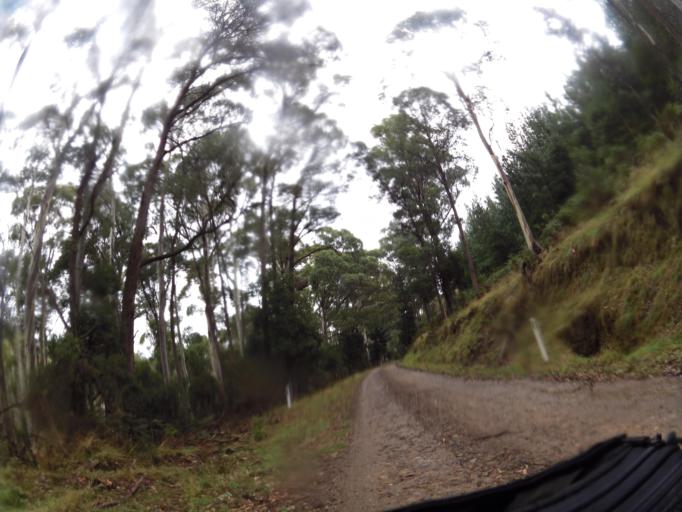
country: AU
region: New South Wales
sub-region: Greater Hume Shire
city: Holbrook
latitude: -36.1990
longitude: 147.5268
